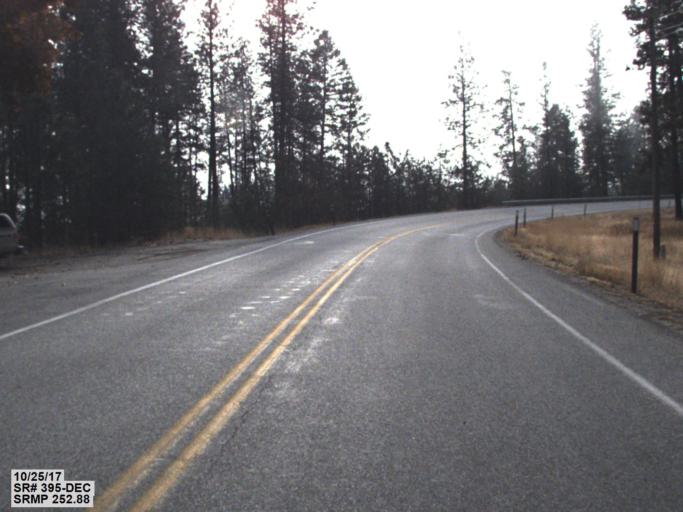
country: US
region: Washington
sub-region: Stevens County
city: Kettle Falls
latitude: 48.7768
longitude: -118.1422
